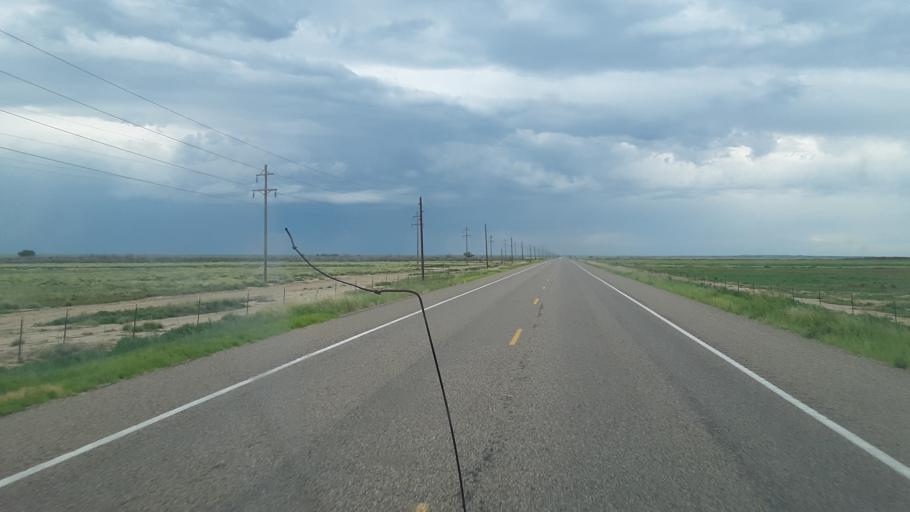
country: US
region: Colorado
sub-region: Crowley County
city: Ordway
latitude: 38.1875
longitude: -103.7482
